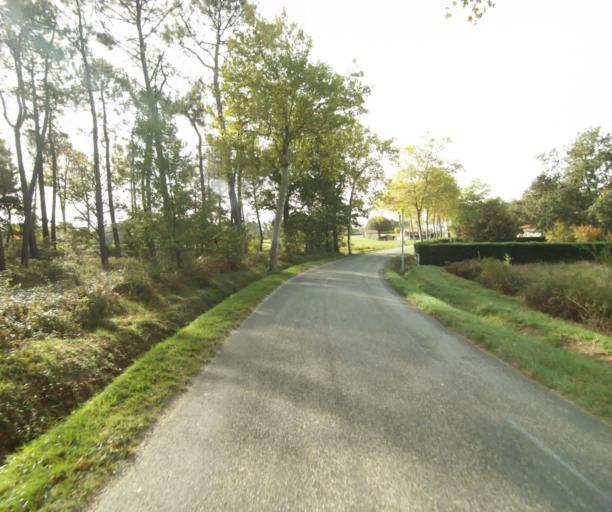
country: FR
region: Midi-Pyrenees
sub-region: Departement du Gers
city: Eauze
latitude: 43.9275
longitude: 0.0913
